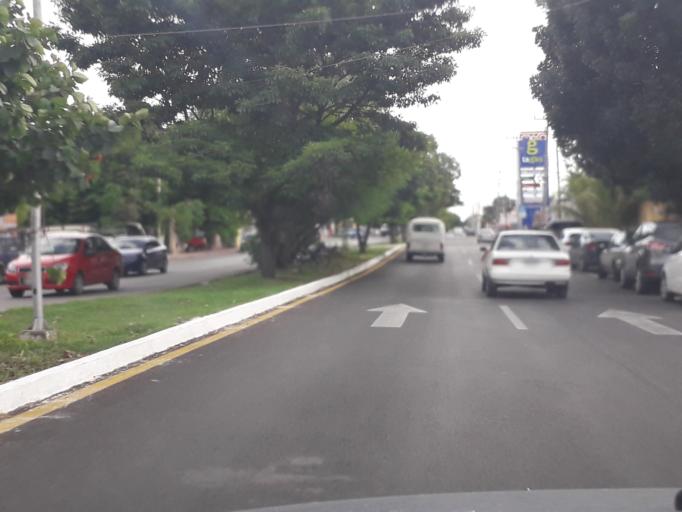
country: MX
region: Yucatan
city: Merida
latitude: 20.9722
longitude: -89.6636
